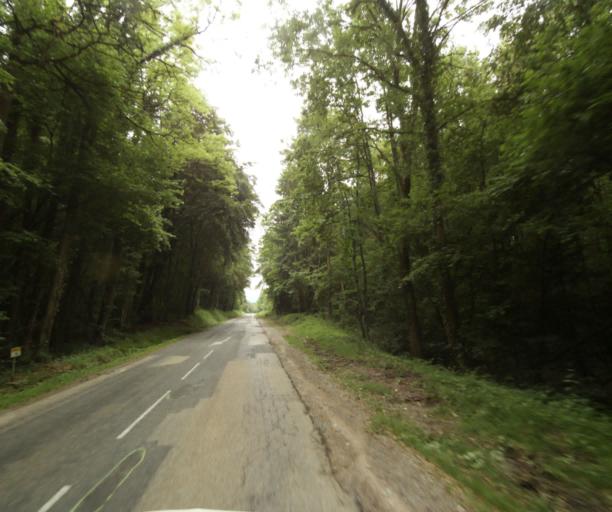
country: FR
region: Rhone-Alpes
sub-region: Departement de la Haute-Savoie
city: Sciez
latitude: 46.3232
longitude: 6.3945
